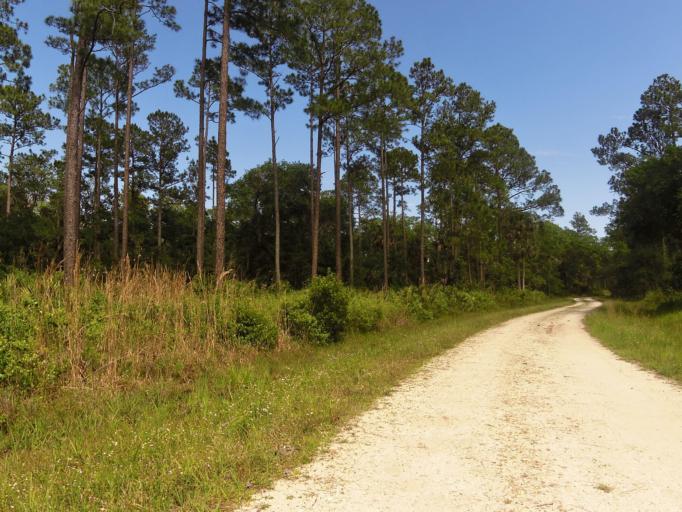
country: US
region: Florida
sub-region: Saint Johns County
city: Palm Valley
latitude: 30.1411
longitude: -81.3742
